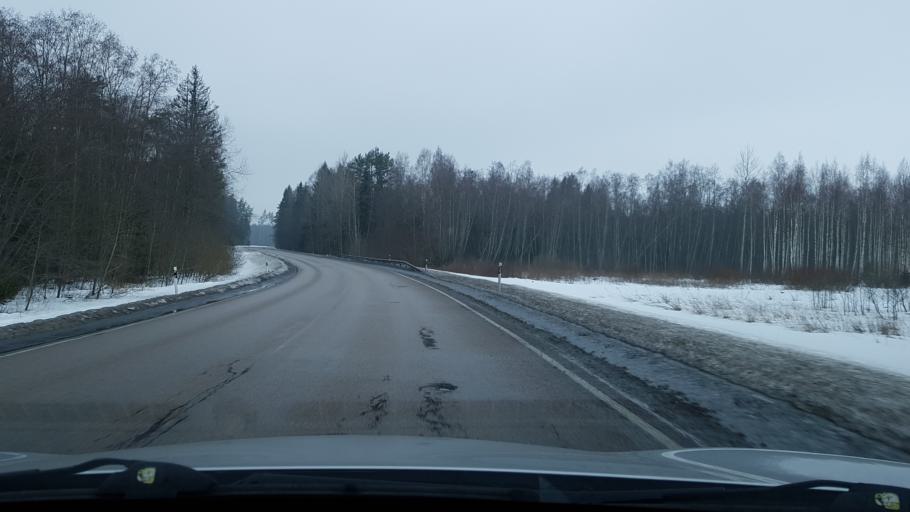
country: EE
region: Valgamaa
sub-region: Torva linn
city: Torva
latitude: 57.9970
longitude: 26.1705
